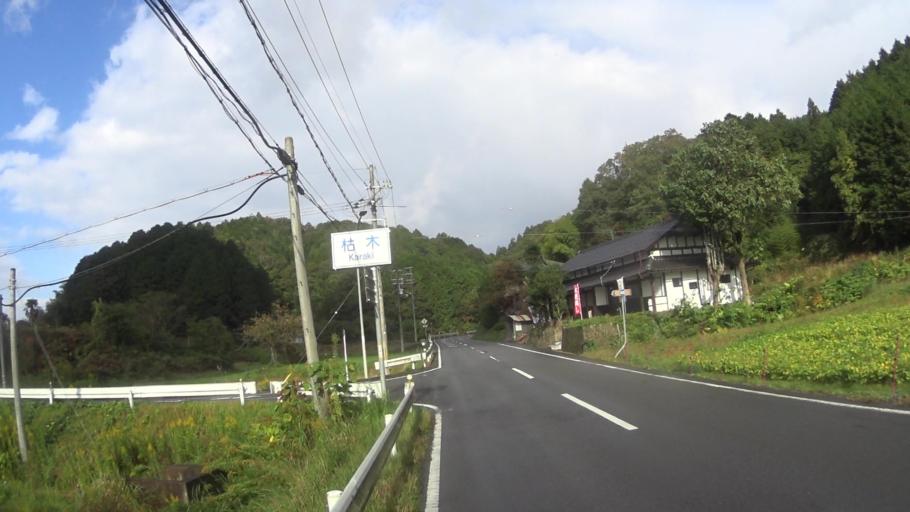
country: JP
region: Kyoto
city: Ayabe
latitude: 35.3692
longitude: 135.1927
